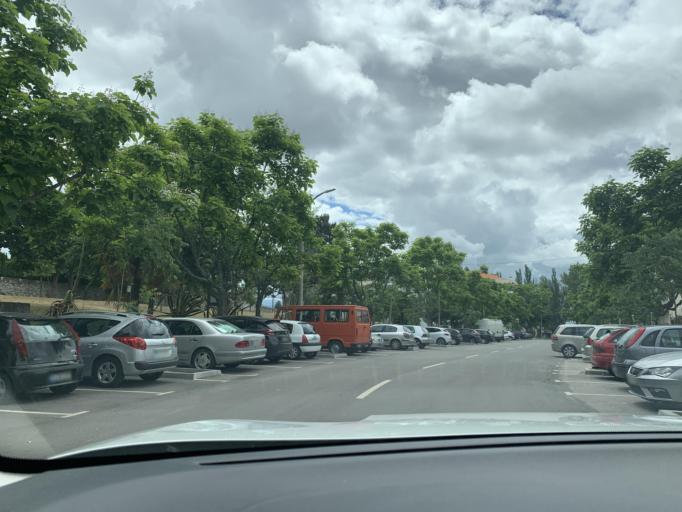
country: PT
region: Viseu
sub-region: Viseu
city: Rio de Loba
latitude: 40.6499
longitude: -7.8903
